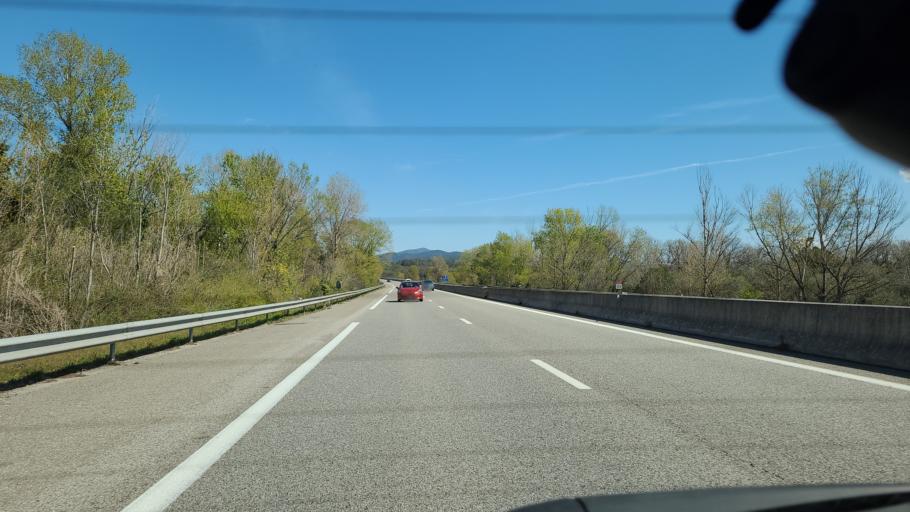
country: FR
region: Provence-Alpes-Cote d'Azur
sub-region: Departement du Var
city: Cuers
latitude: 43.2535
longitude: 6.1101
